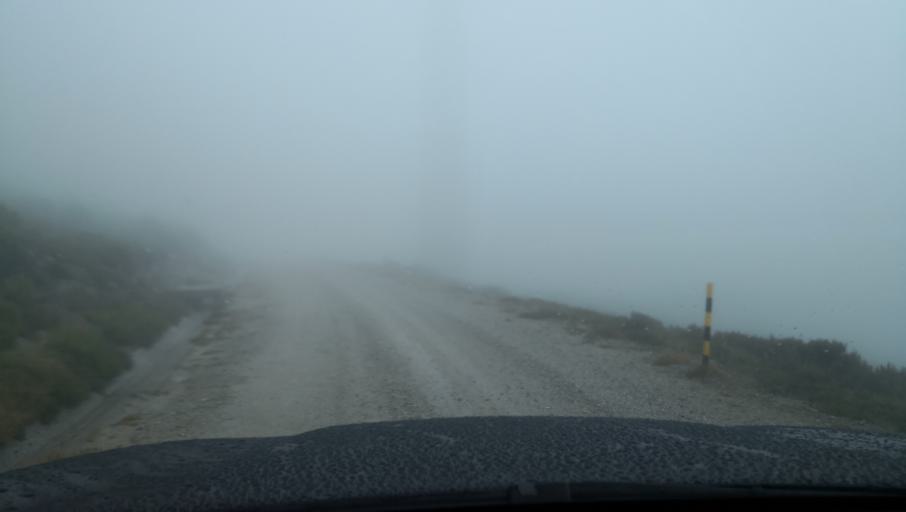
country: PT
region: Vila Real
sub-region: Vila Real
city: Vila Real
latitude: 41.3377
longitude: -7.8463
